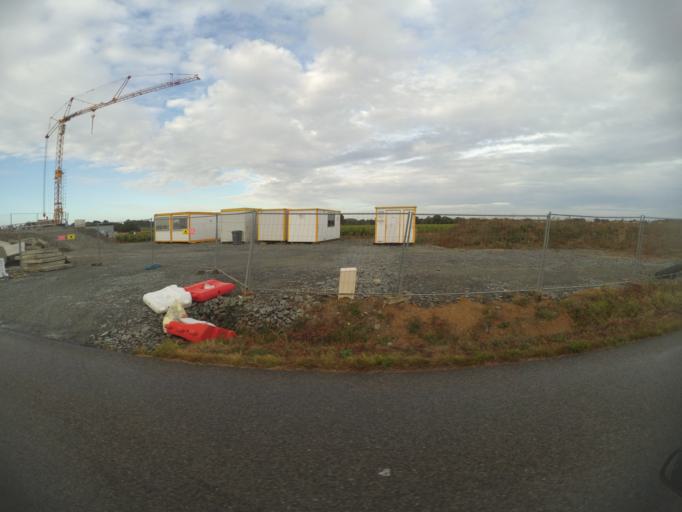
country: FR
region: Pays de la Loire
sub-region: Departement de la Loire-Atlantique
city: Aigrefeuille-sur-Maine
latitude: 47.0667
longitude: -1.4041
